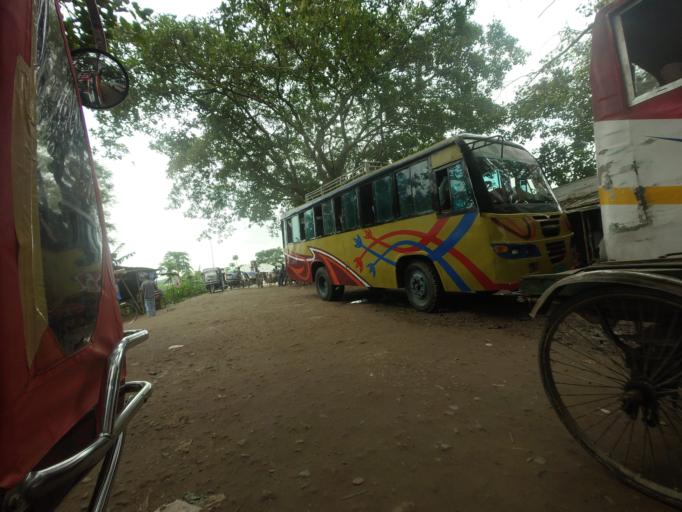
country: BD
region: Khulna
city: Kalia
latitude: 23.1949
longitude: 89.6876
